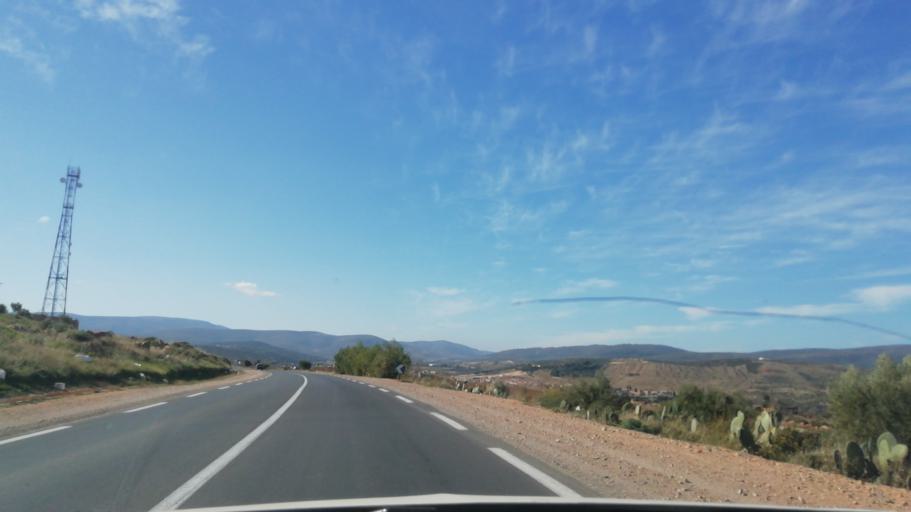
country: DZ
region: Tlemcen
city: Ouled Mimoun
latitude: 34.8769
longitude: -1.1166
